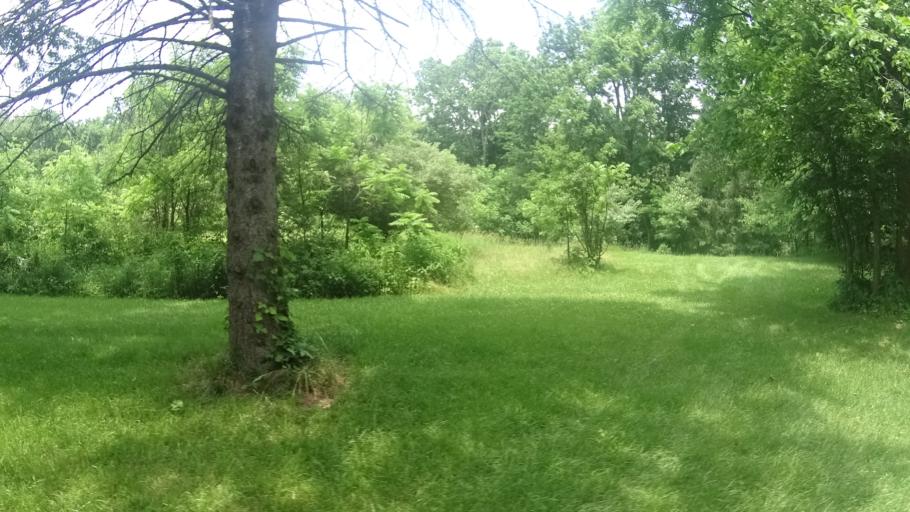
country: US
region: Ohio
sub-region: Erie County
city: Milan
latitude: 41.2993
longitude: -82.6161
